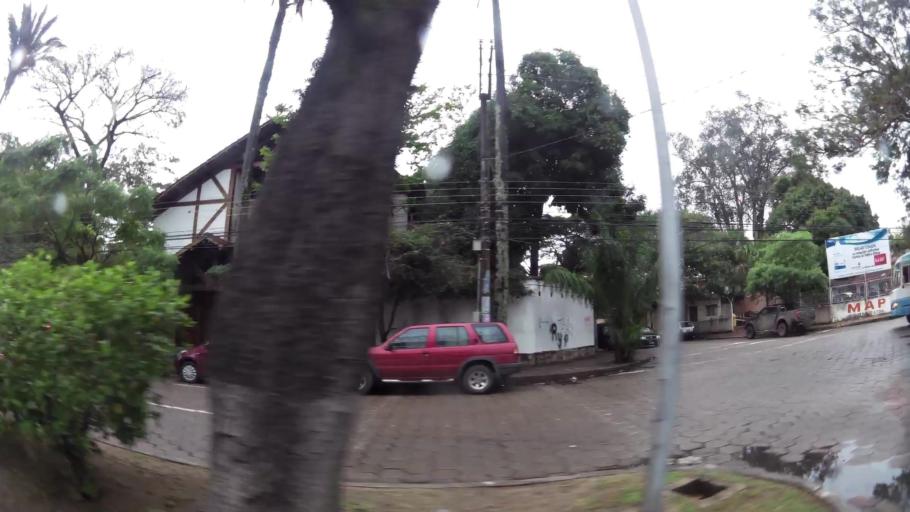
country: BO
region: Santa Cruz
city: Santa Cruz de la Sierra
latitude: -17.7938
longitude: -63.1825
